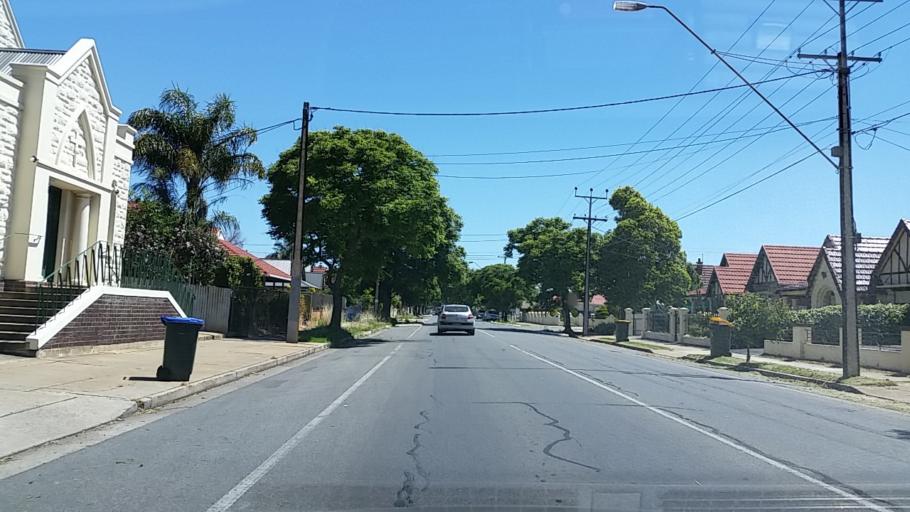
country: AU
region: South Australia
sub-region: Charles Sturt
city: Allenby Gardens
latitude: -34.8892
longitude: 138.5589
